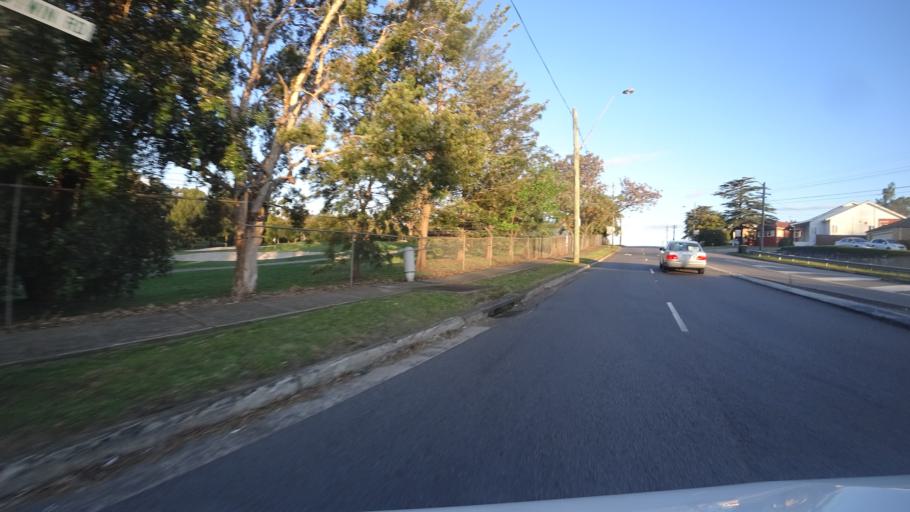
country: AU
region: New South Wales
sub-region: Ryde
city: North Ryde
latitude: -33.7999
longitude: 151.1184
